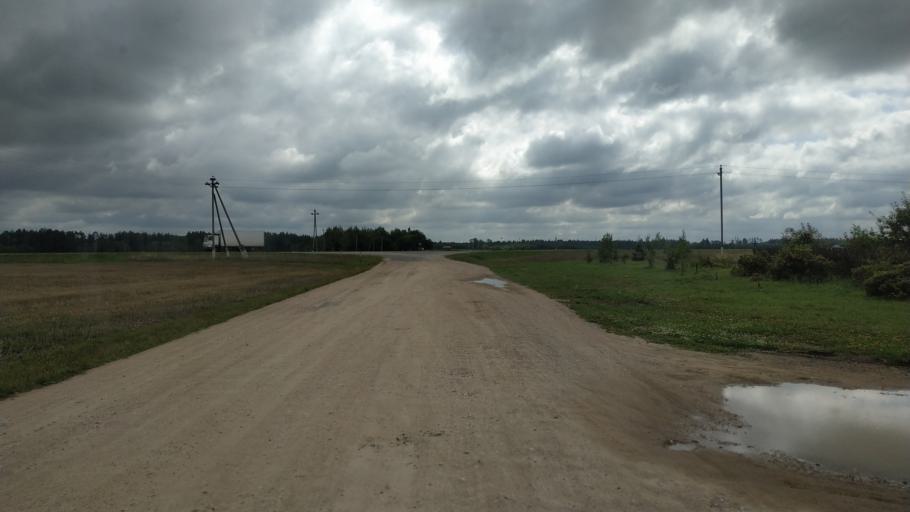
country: BY
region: Mogilev
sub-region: Mahilyowski Rayon
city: Kadino
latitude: 53.8451
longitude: 30.4784
